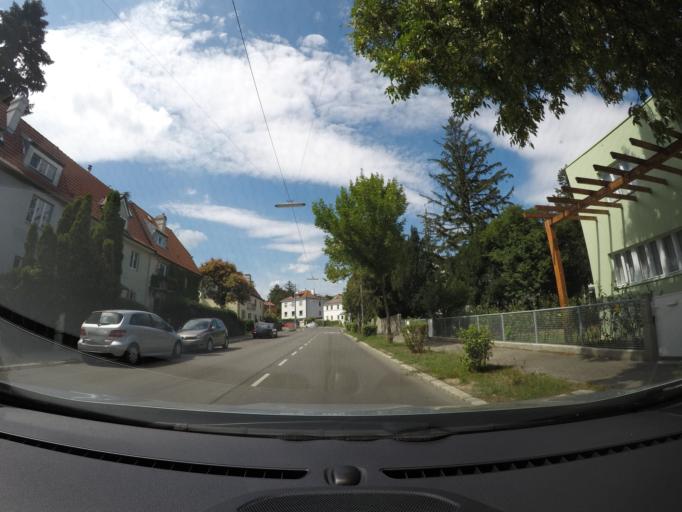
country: AT
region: Lower Austria
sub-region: Politischer Bezirk Modling
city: Perchtoldsdorf
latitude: 48.1803
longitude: 16.2678
